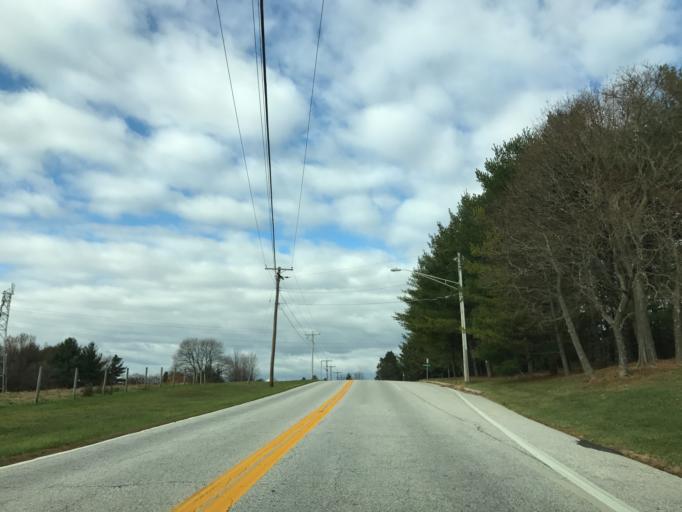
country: US
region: Maryland
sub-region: Harford County
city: Fallston
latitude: 39.5056
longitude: -76.4993
